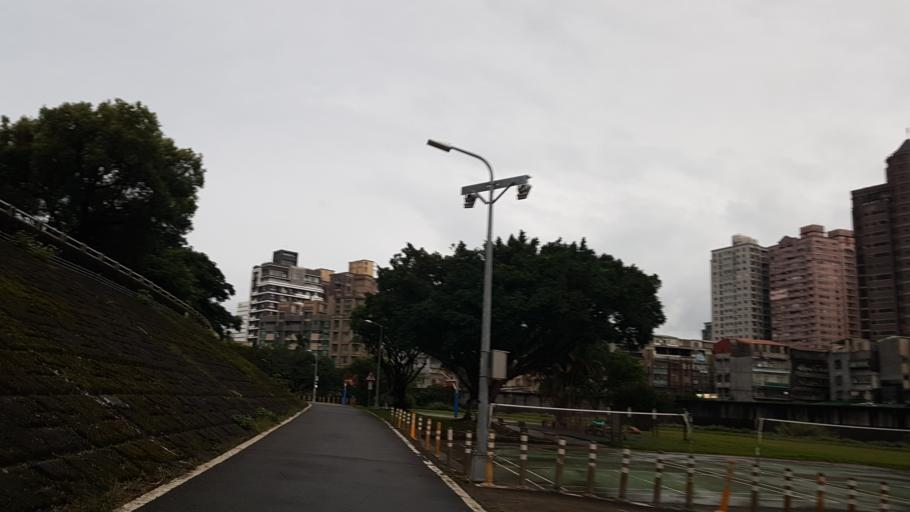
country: TW
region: Taipei
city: Taipei
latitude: 24.9851
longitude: 121.5451
